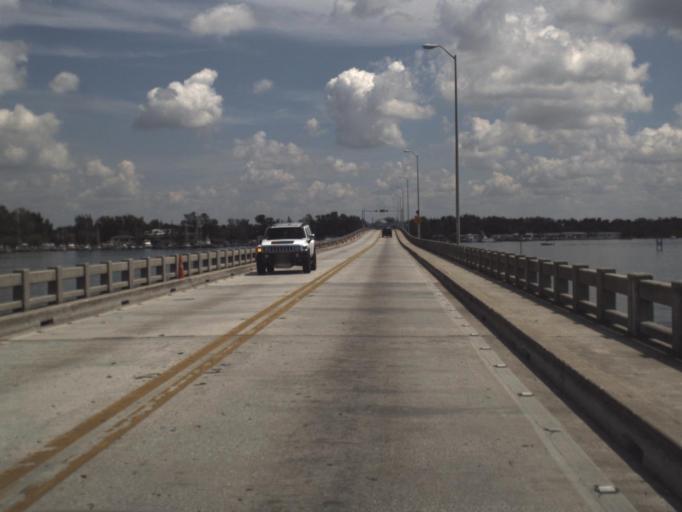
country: US
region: Florida
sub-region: Manatee County
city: Bradenton Beach
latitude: 27.4685
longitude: -82.6961
